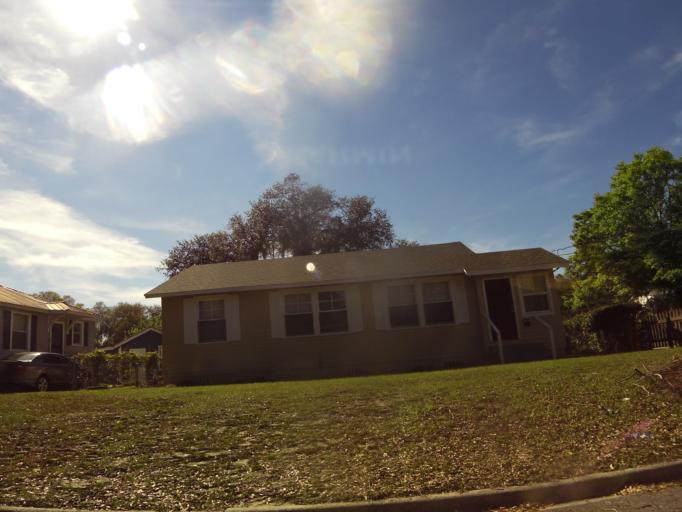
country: US
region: Florida
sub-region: Duval County
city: Jacksonville
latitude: 30.3596
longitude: -81.6516
